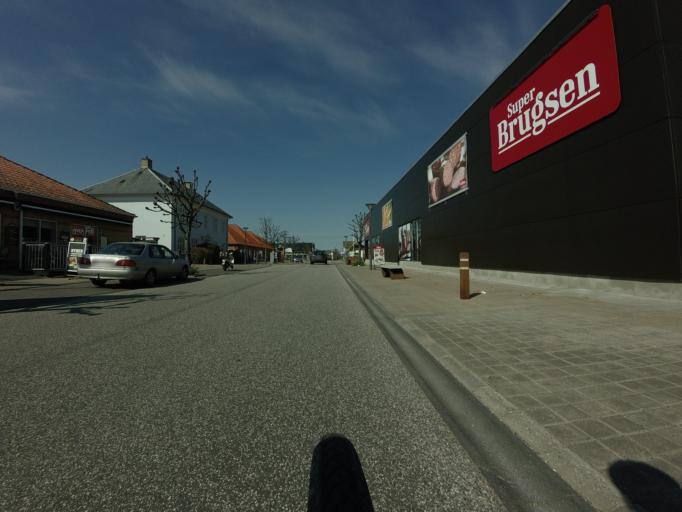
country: DK
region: North Denmark
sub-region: Jammerbugt Kommune
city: Pandrup
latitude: 57.2242
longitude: 9.6770
